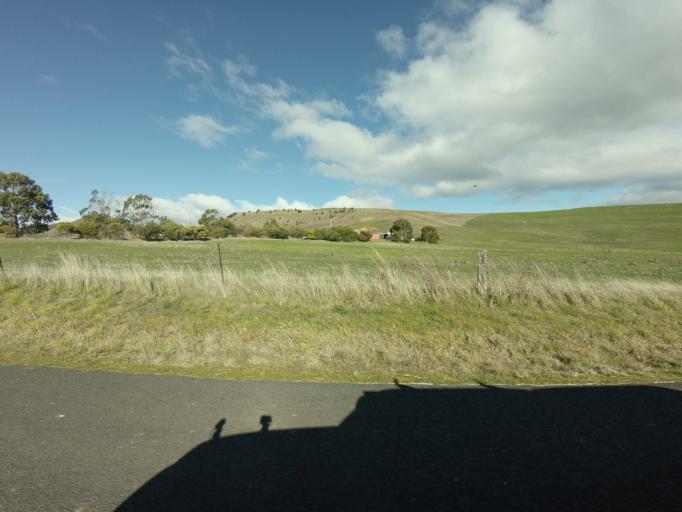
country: AU
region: Tasmania
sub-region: Derwent Valley
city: New Norfolk
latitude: -42.6948
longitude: 146.9627
